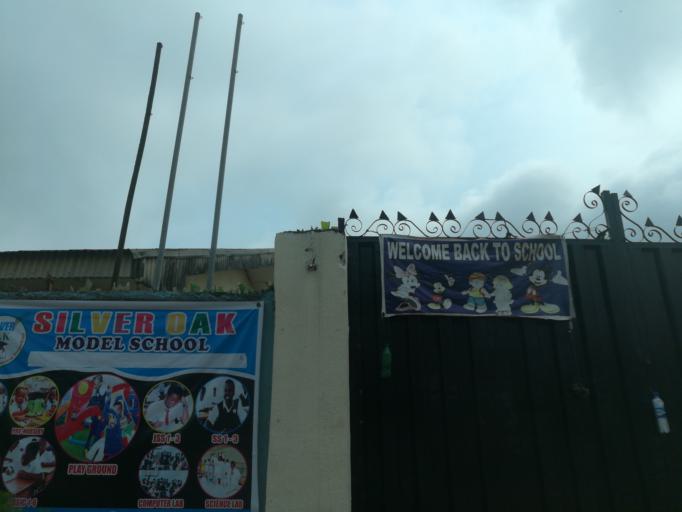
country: NG
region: Rivers
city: Port Harcourt
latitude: 4.8814
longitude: 6.9754
